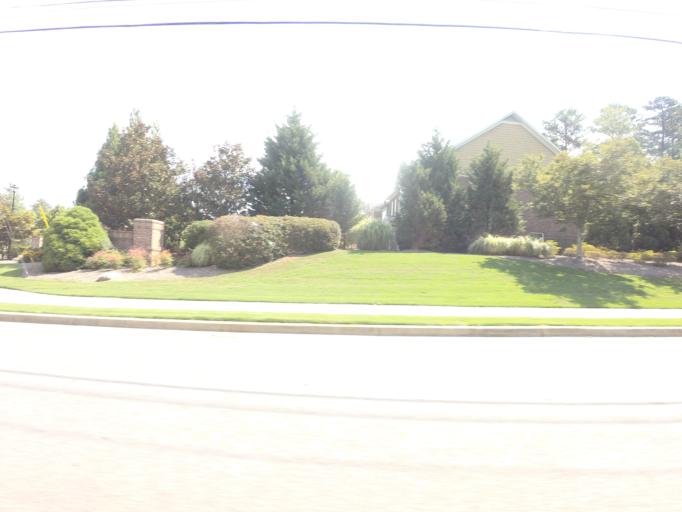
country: US
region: Georgia
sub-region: Fulton County
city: Alpharetta
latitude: 34.0325
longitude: -84.2714
